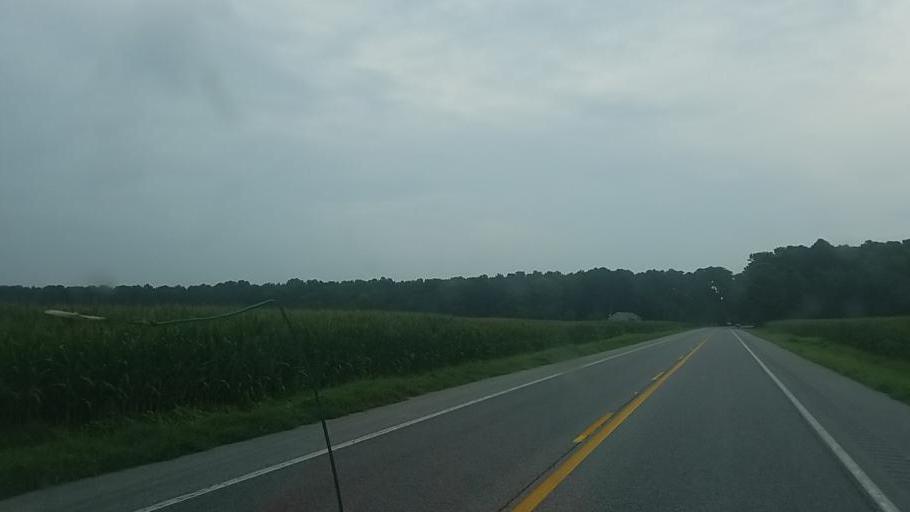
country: US
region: Delaware
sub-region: Sussex County
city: Selbyville
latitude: 38.4386
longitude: -75.2329
